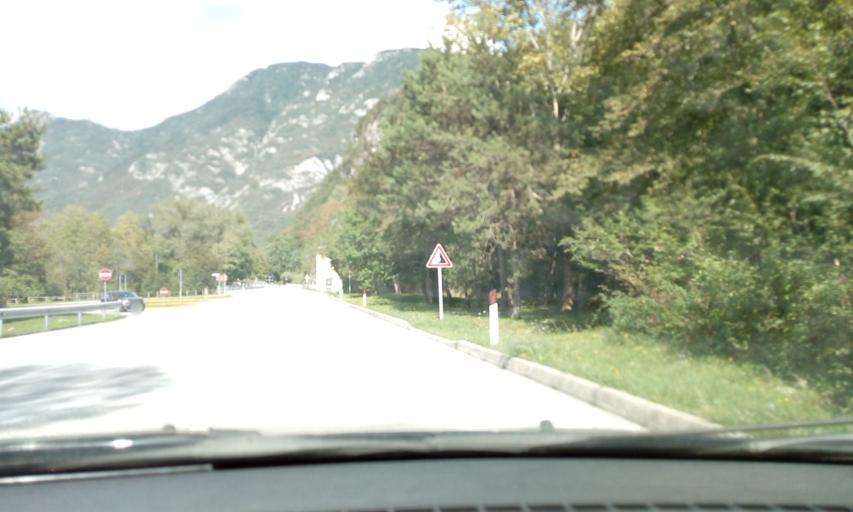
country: IT
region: Friuli Venezia Giulia
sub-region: Provincia di Udine
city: Trasaghis
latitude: 46.3169
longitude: 13.0665
